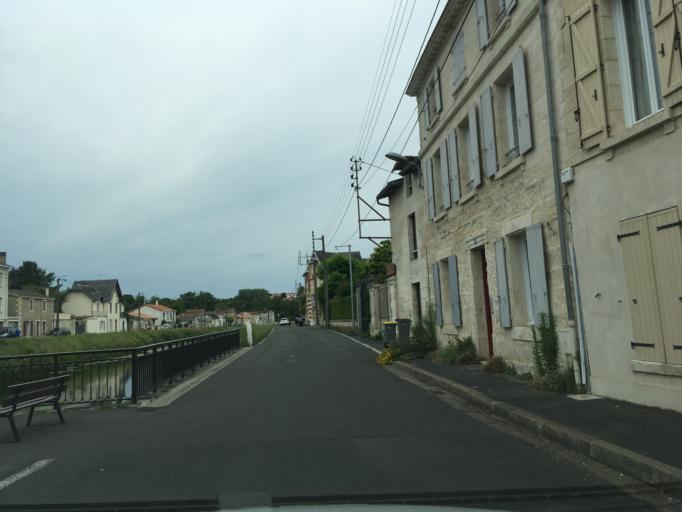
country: FR
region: Poitou-Charentes
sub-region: Departement des Deux-Sevres
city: Niort
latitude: 46.3254
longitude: -0.4713
